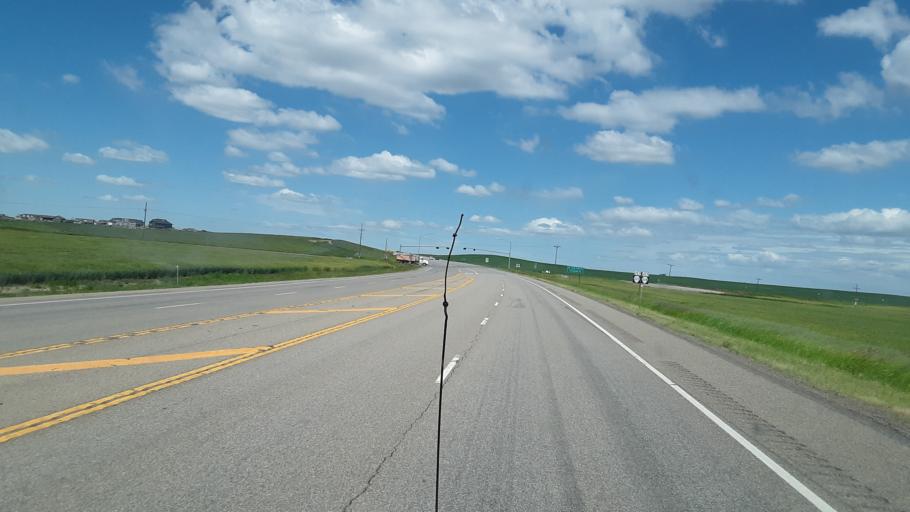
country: US
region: Montana
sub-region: Cascade County
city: Malmstrom Air Force Base
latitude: 47.4780
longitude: -111.1526
